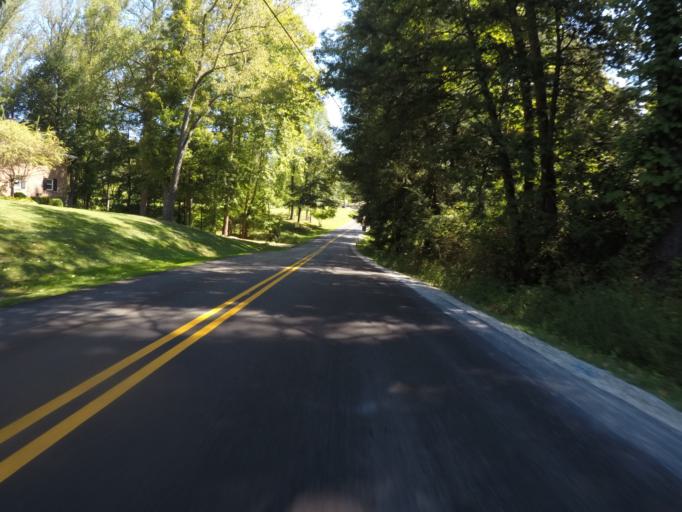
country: US
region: Kentucky
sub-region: Boyd County
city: Ashland
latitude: 38.4483
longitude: -82.6388
